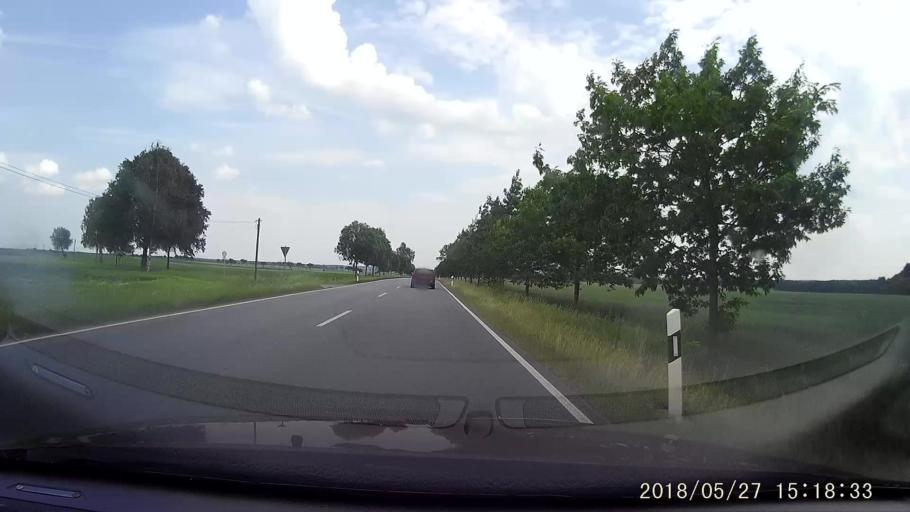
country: DE
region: Saxony
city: Kodersdorf
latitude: 51.2642
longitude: 14.8581
